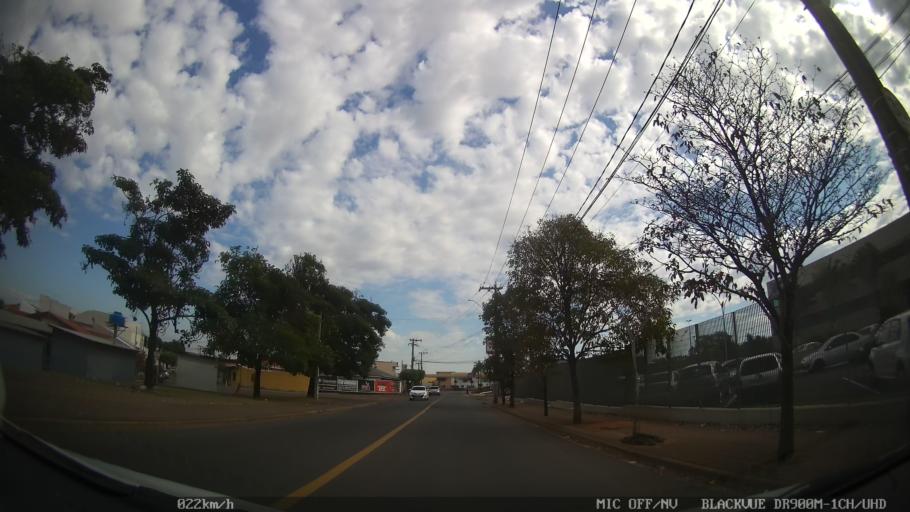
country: BR
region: Sao Paulo
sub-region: Americana
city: Americana
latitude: -22.7397
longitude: -47.3625
